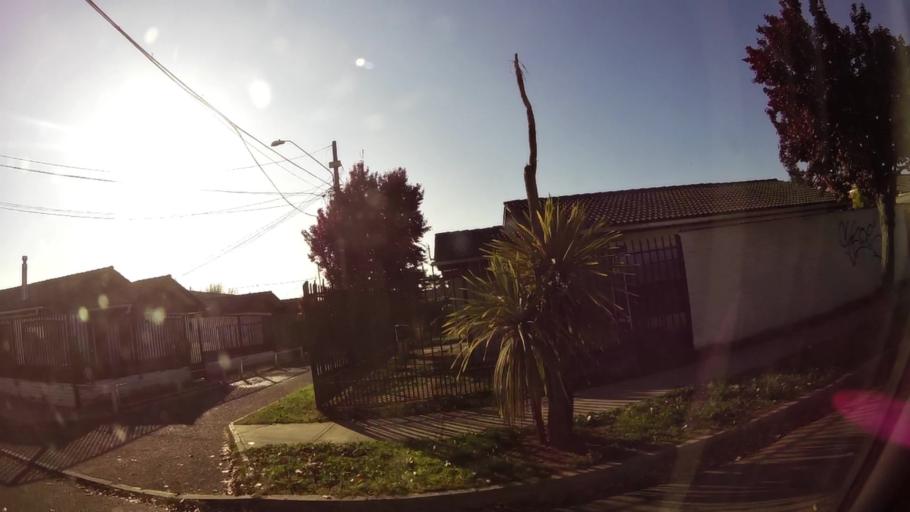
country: CL
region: Santiago Metropolitan
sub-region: Provincia de Santiago
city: Lo Prado
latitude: -33.4863
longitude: -70.7616
